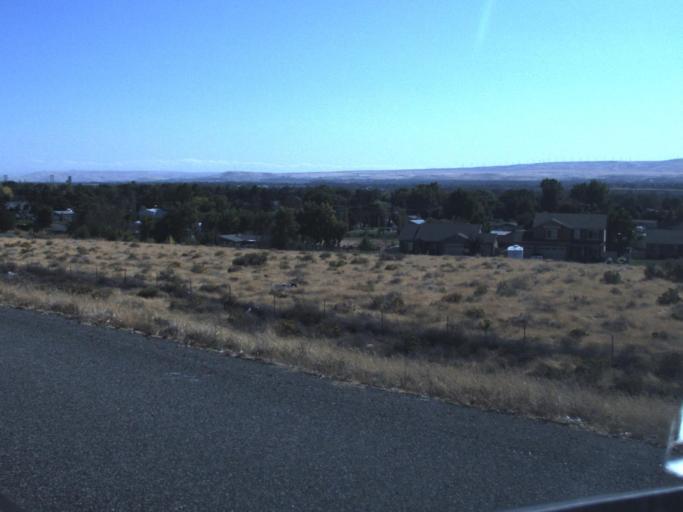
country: US
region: Washington
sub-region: Franklin County
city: West Pasco
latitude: 46.2591
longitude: -119.1618
